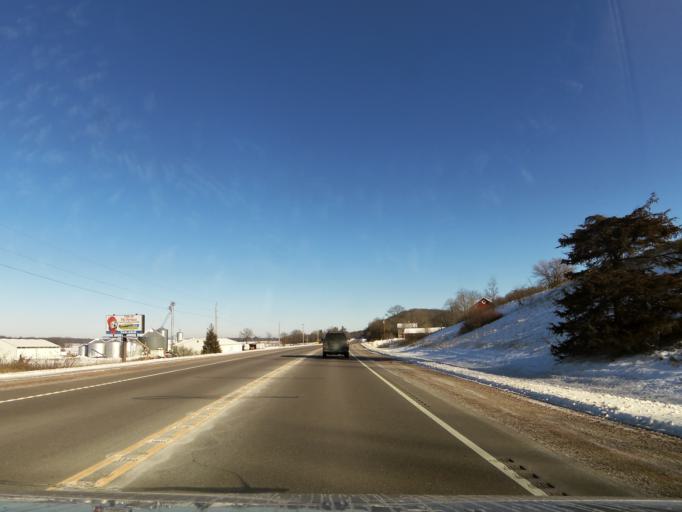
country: US
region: Wisconsin
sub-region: Columbia County
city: Lake Wisconsin
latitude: 43.5070
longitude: -89.5966
